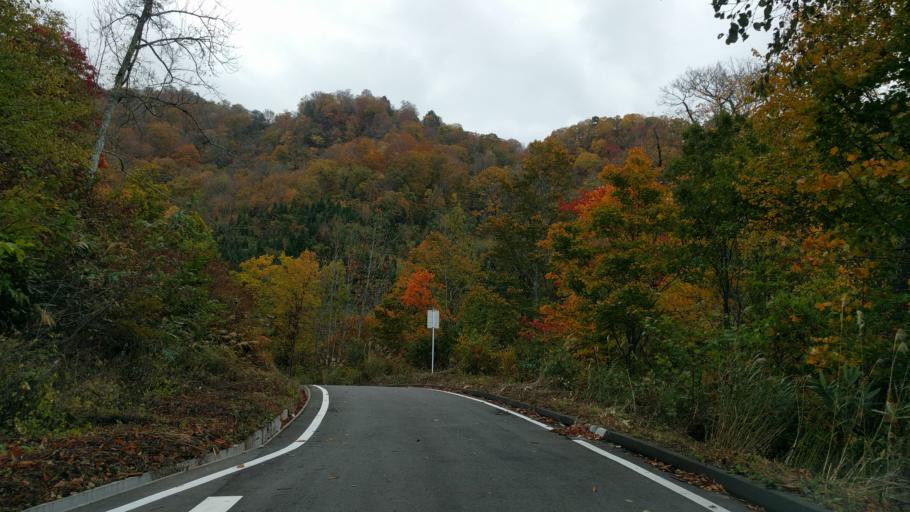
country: JP
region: Fukushima
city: Kitakata
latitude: 37.3806
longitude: 139.6969
